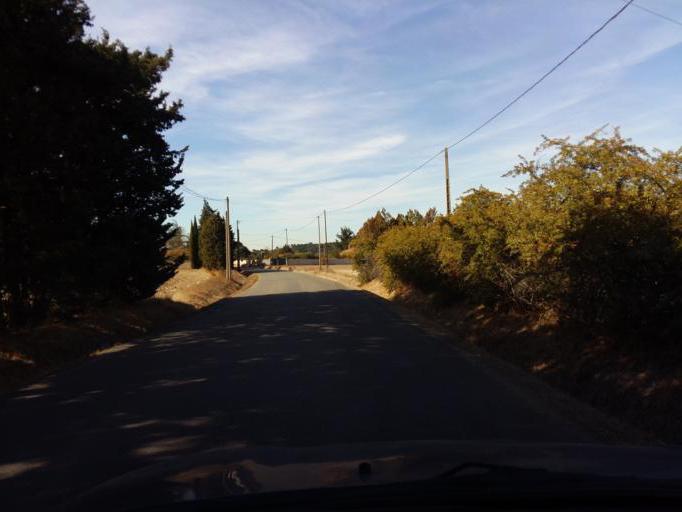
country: FR
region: Provence-Alpes-Cote d'Azur
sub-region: Departement du Vaucluse
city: Piolenc
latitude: 44.1809
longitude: 4.7839
